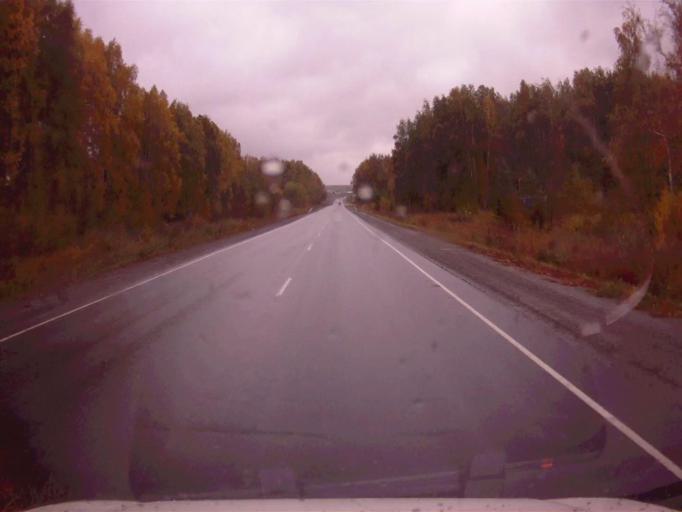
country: RU
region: Chelyabinsk
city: Roshchino
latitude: 55.3635
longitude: 61.2074
